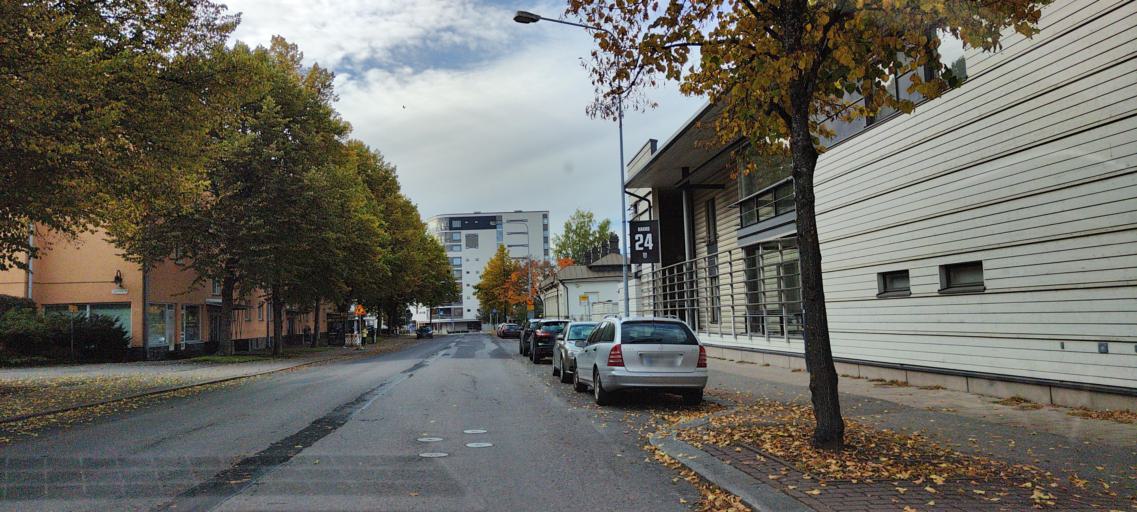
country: FI
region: Varsinais-Suomi
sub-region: Turku
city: Turku
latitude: 60.4450
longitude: 22.2390
